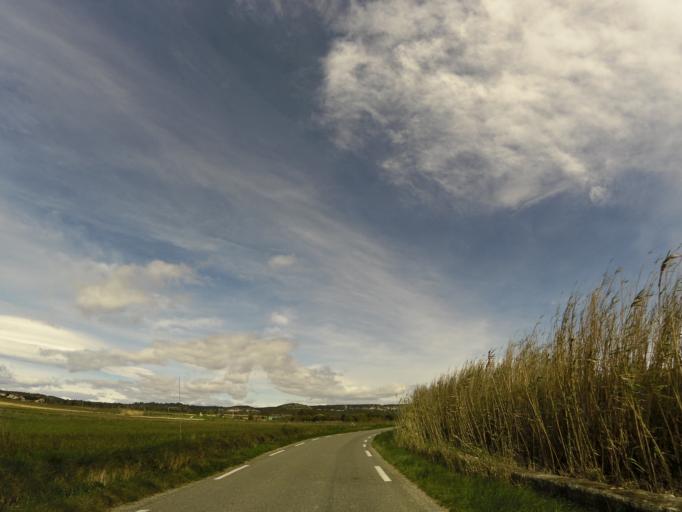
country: FR
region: Languedoc-Roussillon
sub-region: Departement du Gard
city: Calvisson
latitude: 43.8073
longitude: 4.1972
